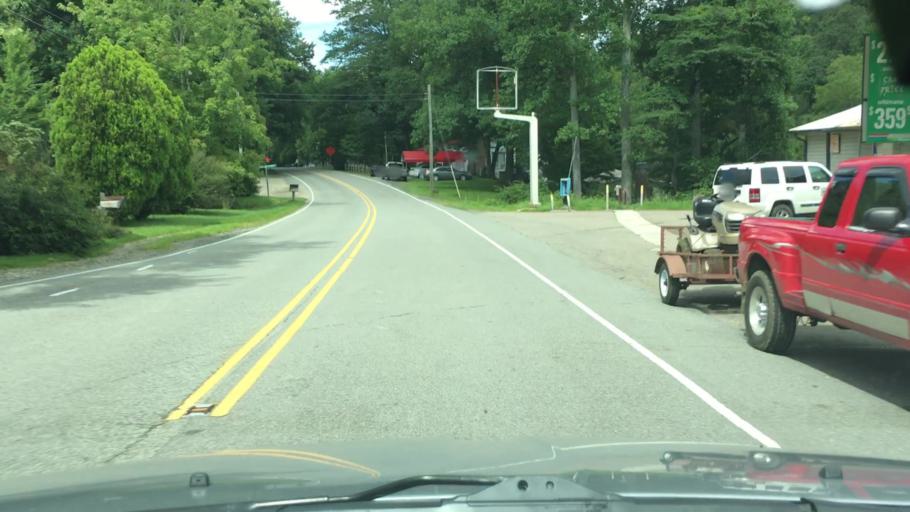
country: US
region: North Carolina
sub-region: Yancey County
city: Burnsville
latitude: 35.8074
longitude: -82.2001
